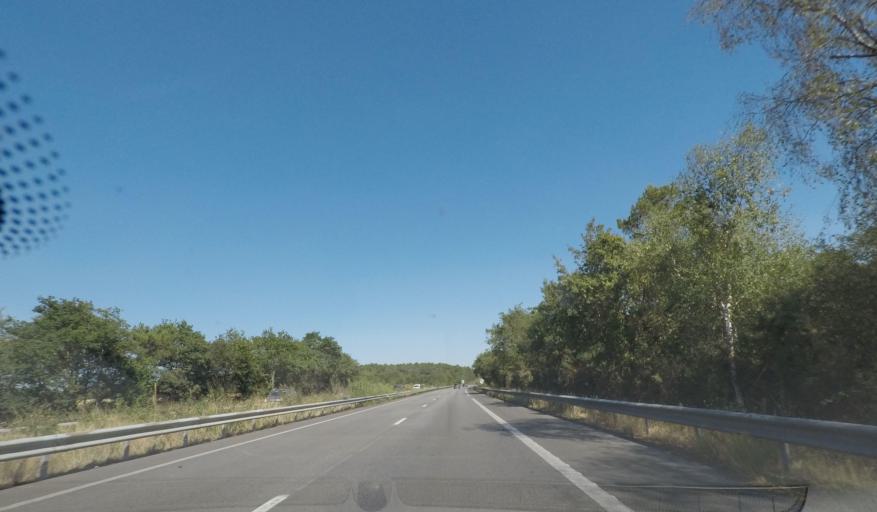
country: FR
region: Brittany
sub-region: Departement du Morbihan
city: Marzan
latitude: 47.5382
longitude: -2.3623
